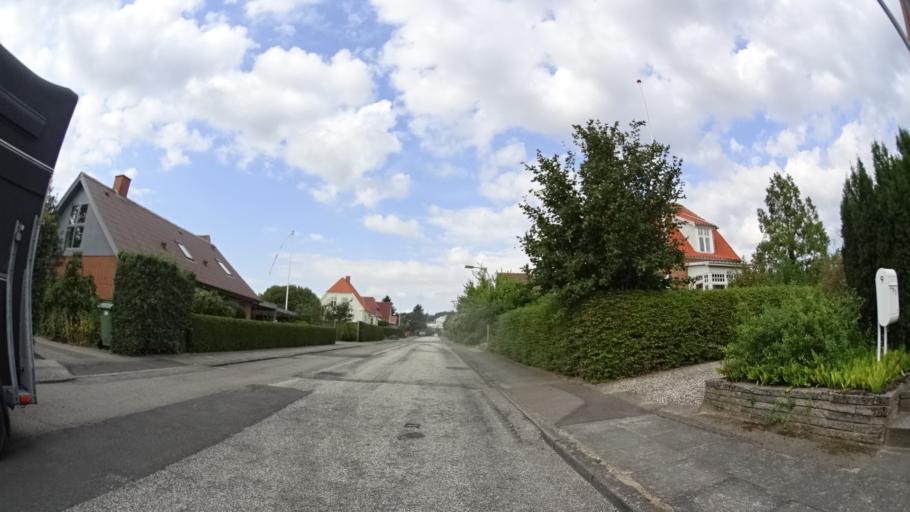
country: DK
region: Central Jutland
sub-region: Arhus Kommune
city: Stavtrup
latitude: 56.1517
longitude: 10.0975
